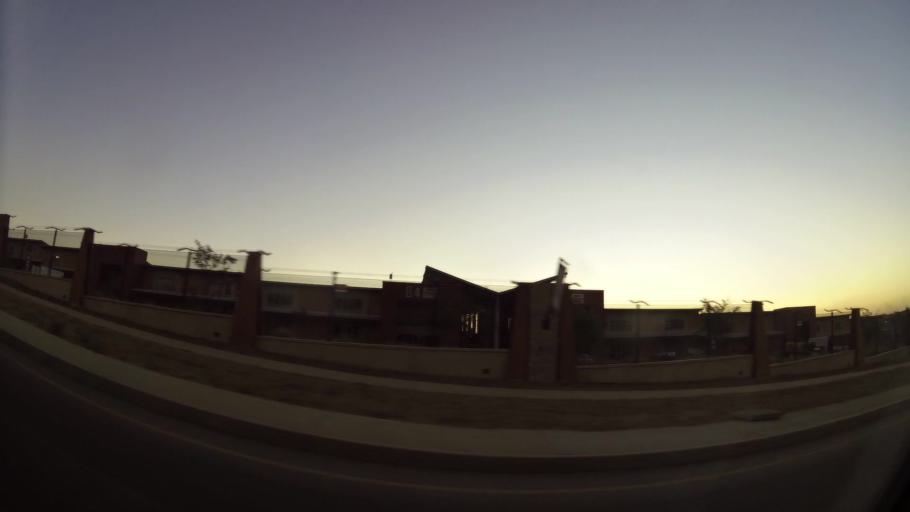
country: ZA
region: Gauteng
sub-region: City of Johannesburg Metropolitan Municipality
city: Diepsloot
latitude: -25.9642
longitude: 28.0248
